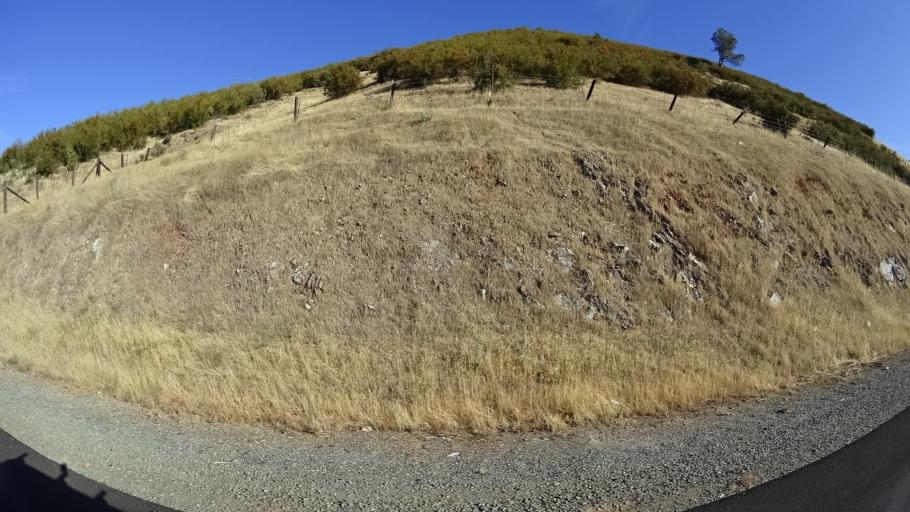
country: US
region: California
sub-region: Calaveras County
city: Valley Springs
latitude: 38.1983
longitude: -120.7996
